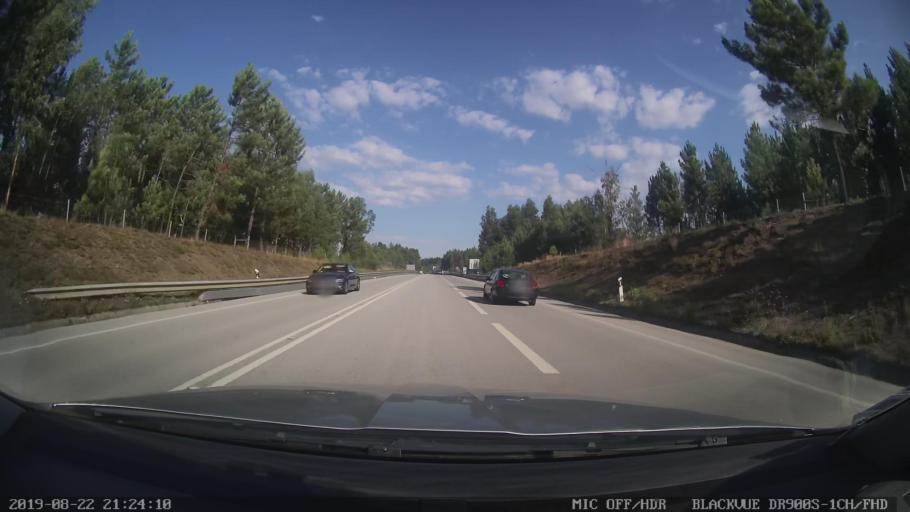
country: PT
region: Castelo Branco
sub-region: Serta
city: Serta
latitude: 39.8387
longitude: -8.1184
